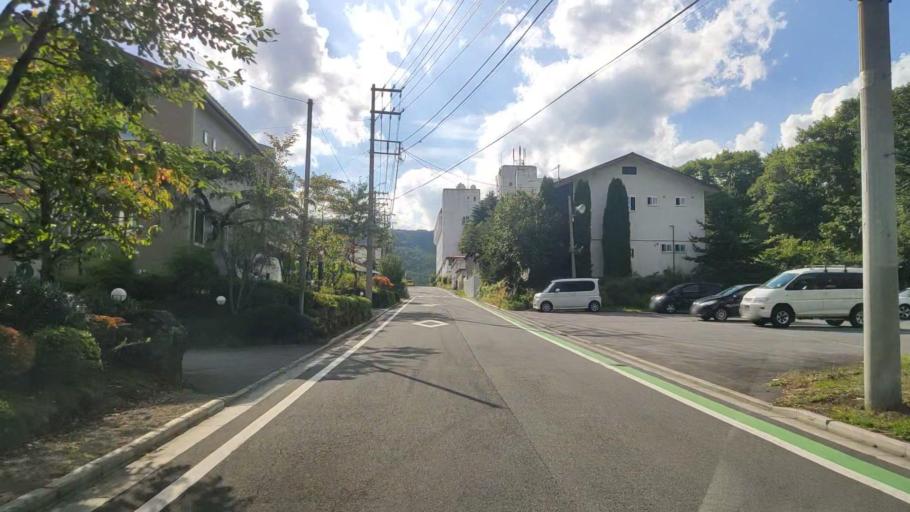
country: JP
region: Gunma
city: Nakanojomachi
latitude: 36.6184
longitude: 138.5979
